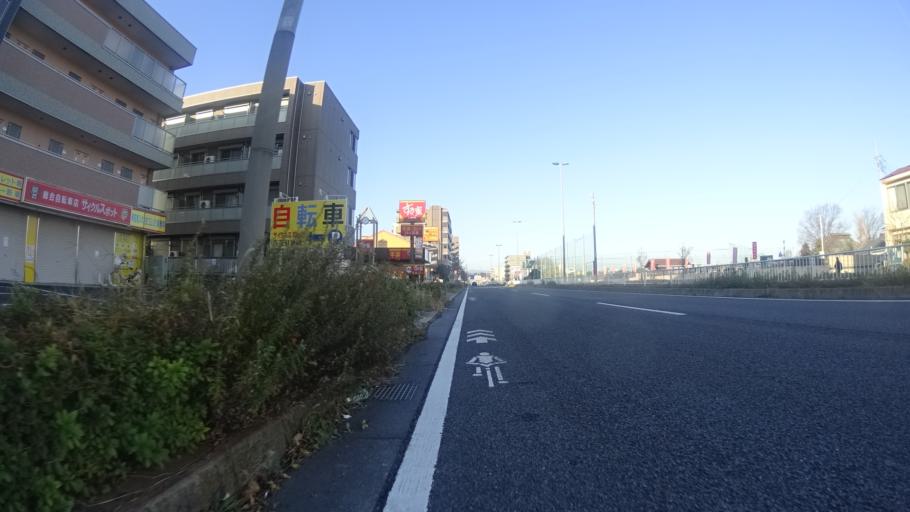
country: JP
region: Tokyo
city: Hino
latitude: 35.6699
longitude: 139.4158
